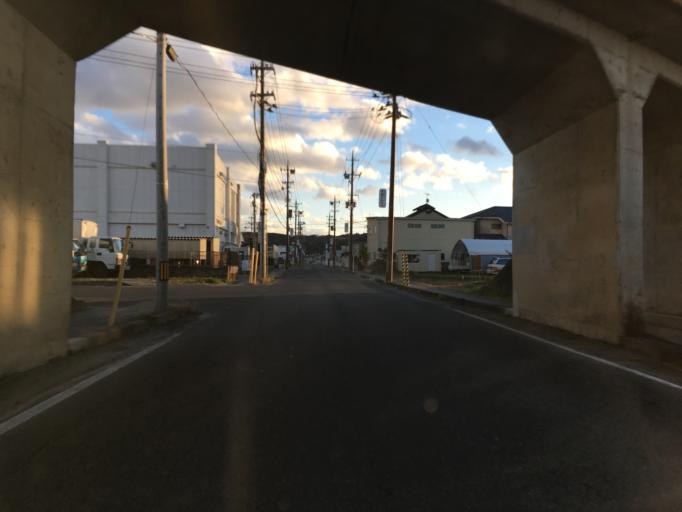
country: JP
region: Fukushima
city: Hobaramachi
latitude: 37.8123
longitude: 140.5517
